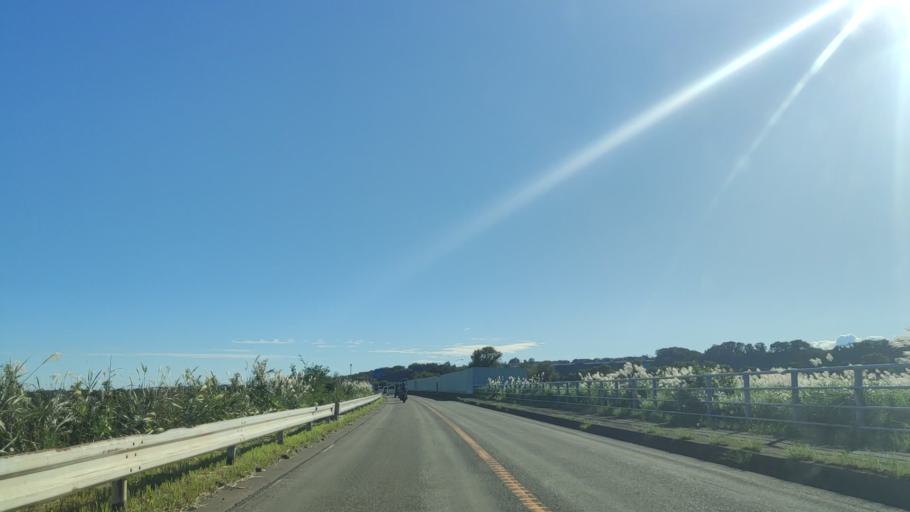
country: JP
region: Kanagawa
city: Zama
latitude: 35.5054
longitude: 139.3732
